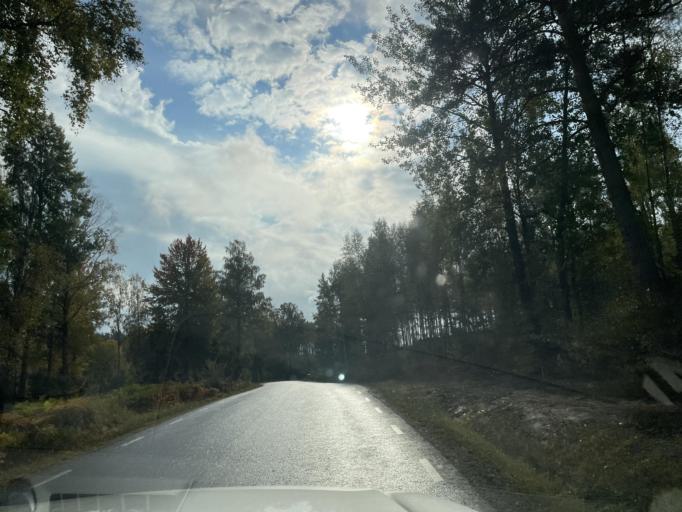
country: SE
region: Vaermland
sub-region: Karlstads Kommun
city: Skattkarr
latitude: 59.4232
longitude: 13.6053
